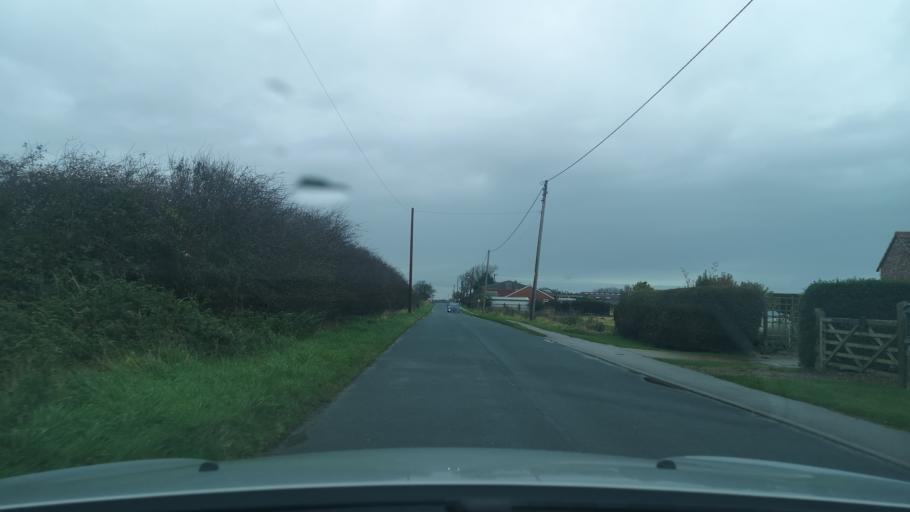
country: GB
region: England
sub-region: East Riding of Yorkshire
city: Easington
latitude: 53.6231
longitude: 0.1276
